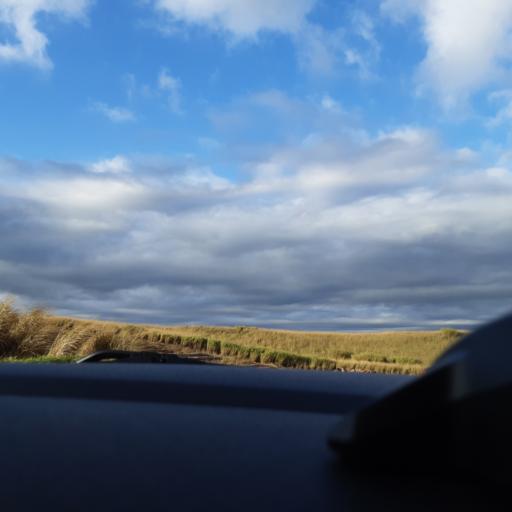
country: BR
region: Sao Paulo
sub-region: Ourinhos
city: Ourinhos
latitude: -23.0029
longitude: -49.8385
